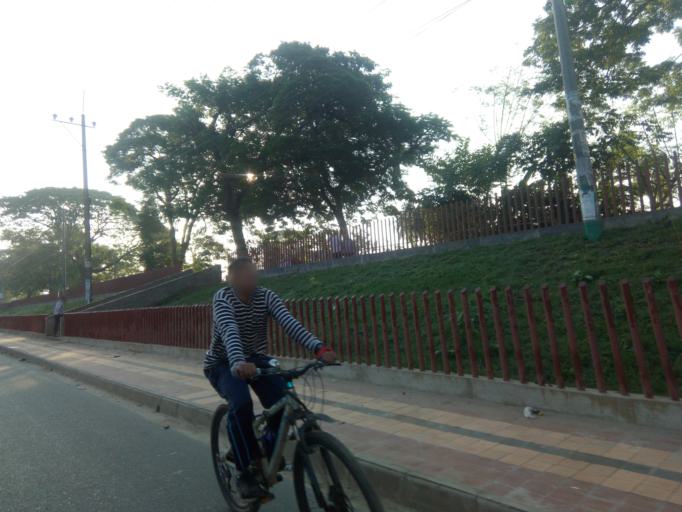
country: BD
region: Rajshahi
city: Rajshahi
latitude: 24.3615
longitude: 88.6112
